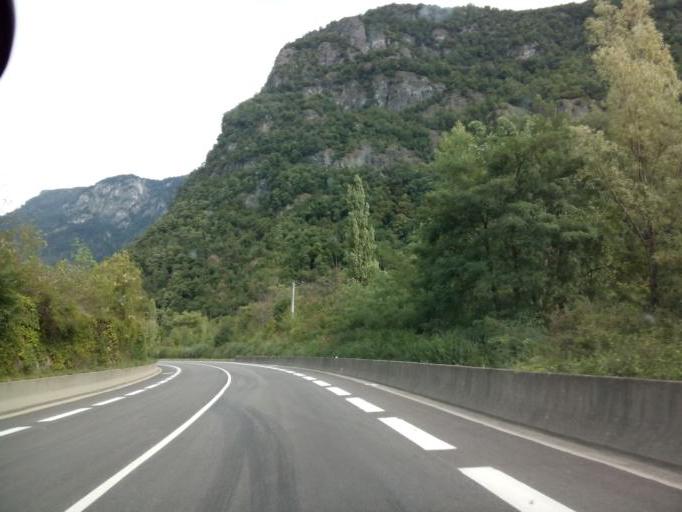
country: FR
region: Rhone-Alpes
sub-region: Departement de l'Isere
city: Vaulnaveys-le-Bas
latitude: 45.0517
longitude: 5.8337
